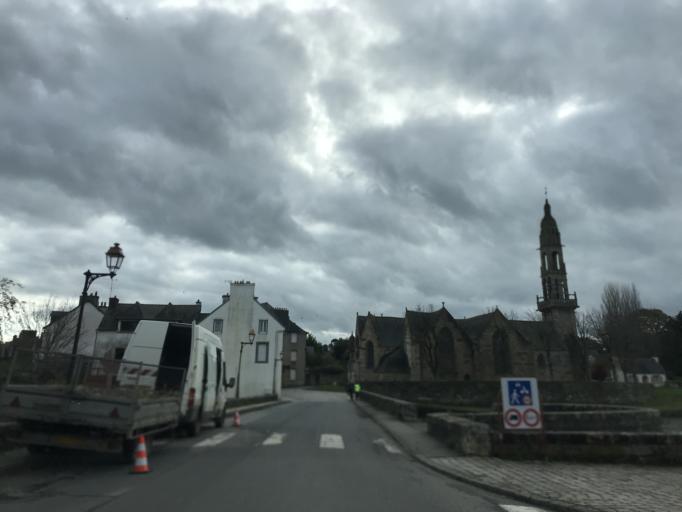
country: FR
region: Brittany
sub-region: Departement du Finistere
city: Le Faou
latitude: 48.2966
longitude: -4.1810
